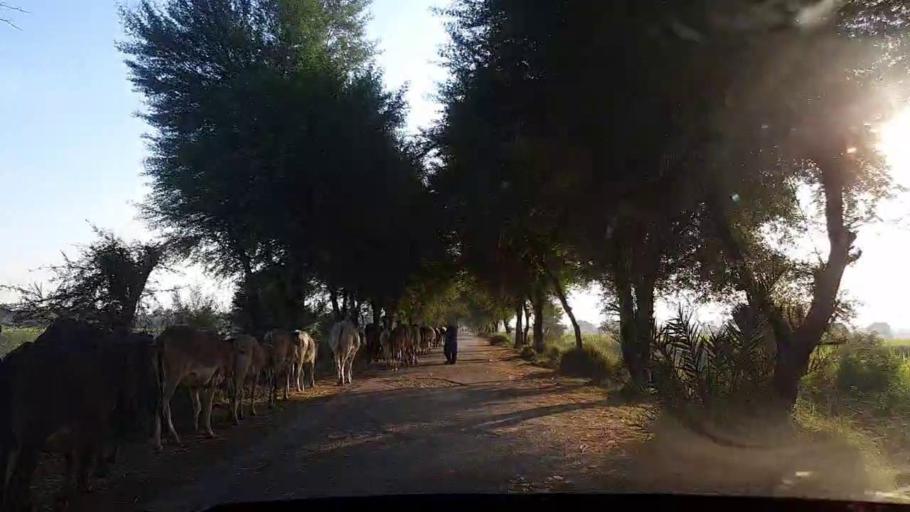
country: PK
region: Sindh
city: Sobhadero
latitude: 27.4066
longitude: 68.3924
